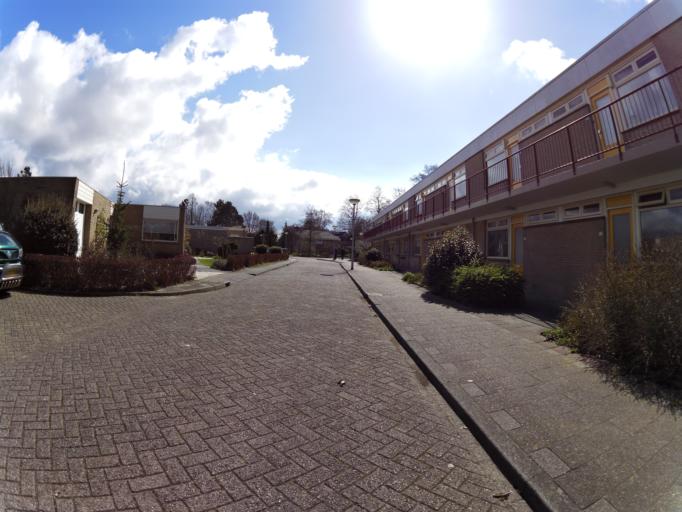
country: NL
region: South Holland
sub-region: Gemeente Hellevoetsluis
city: Nieuw-Helvoet
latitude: 51.8755
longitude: 4.0596
